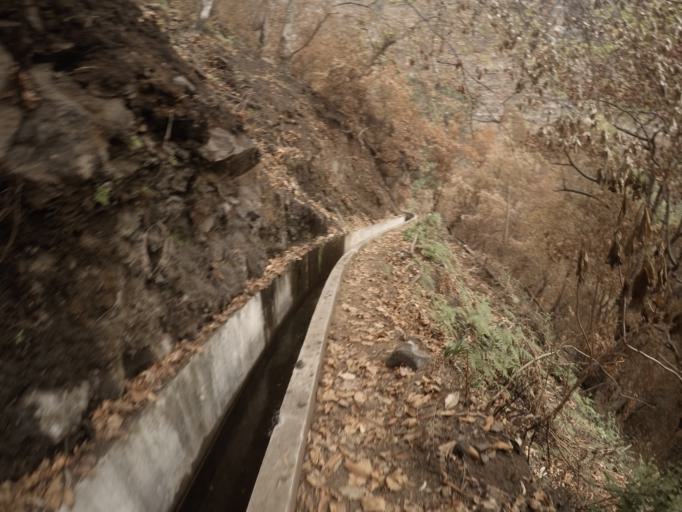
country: PT
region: Madeira
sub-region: Funchal
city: Nossa Senhora do Monte
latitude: 32.6887
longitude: -16.9121
